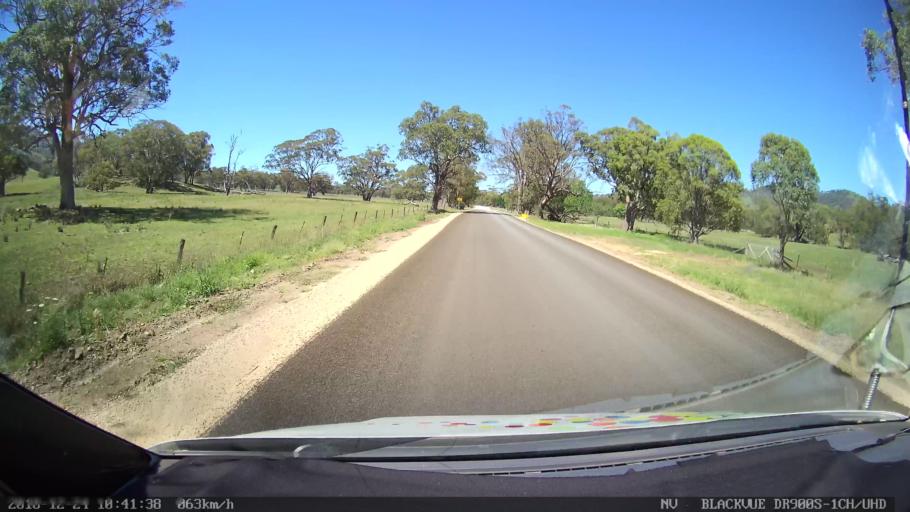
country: AU
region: New South Wales
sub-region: Upper Hunter Shire
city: Merriwa
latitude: -31.8706
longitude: 150.4578
